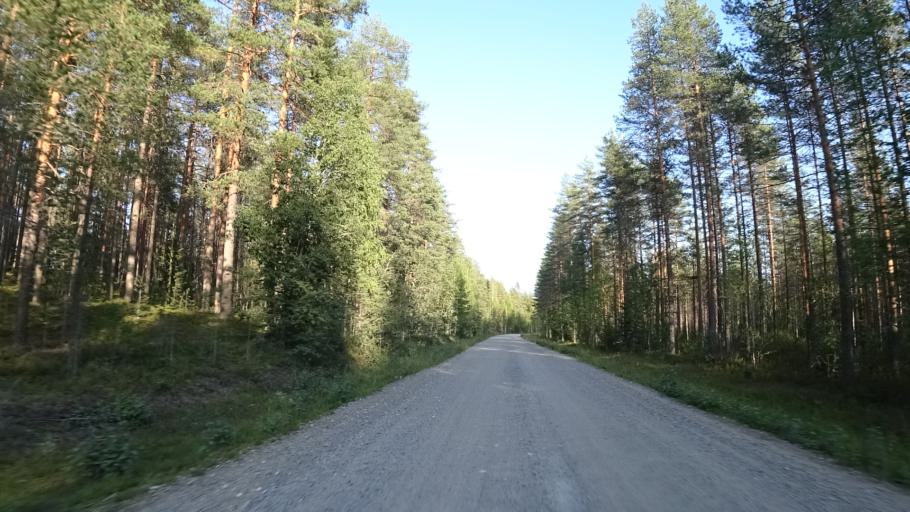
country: FI
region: North Karelia
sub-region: Joensuu
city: Ilomantsi
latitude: 63.1376
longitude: 30.7003
